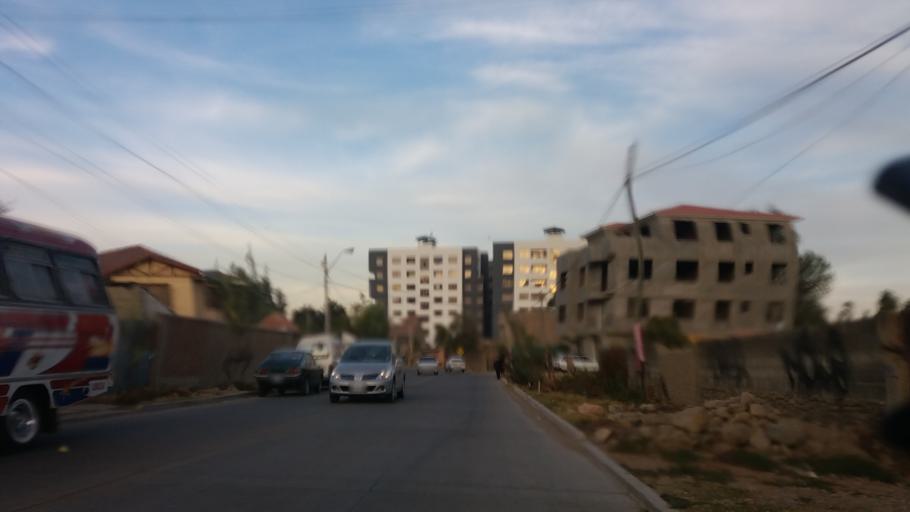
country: BO
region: Cochabamba
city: Cochabamba
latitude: -17.3751
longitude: -66.1957
